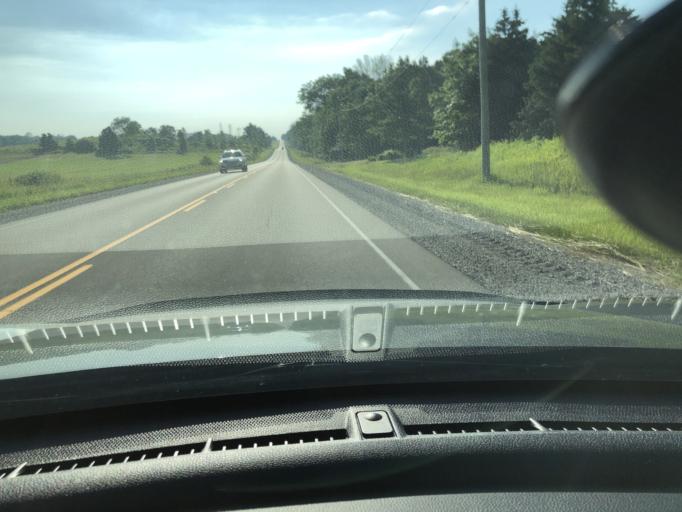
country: CA
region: Ontario
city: Stratford
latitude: 43.4244
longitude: -80.7818
